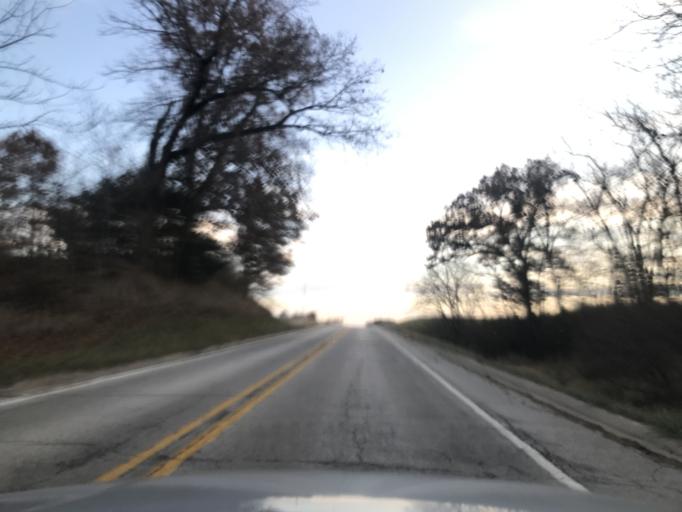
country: US
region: Illinois
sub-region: Henderson County
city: Oquawka
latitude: 40.9592
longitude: -90.8640
